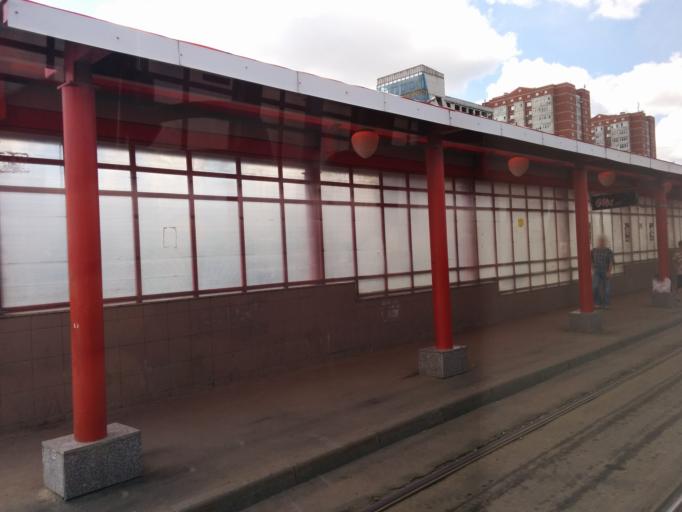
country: RU
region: Tatarstan
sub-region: Gorod Kazan'
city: Kazan
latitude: 55.8270
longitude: 49.1220
